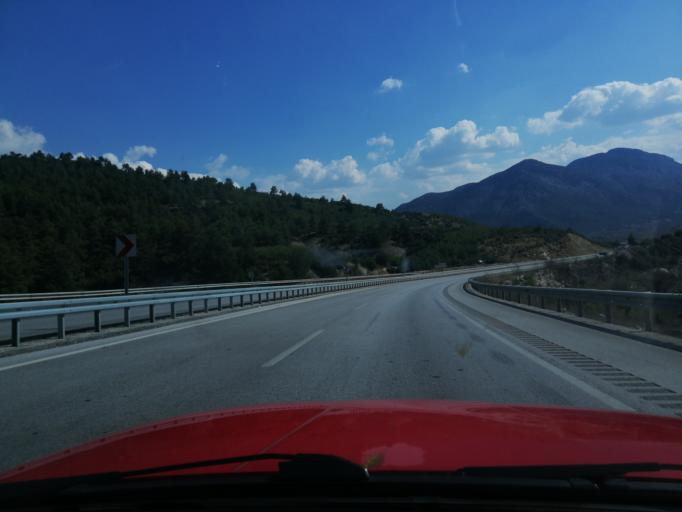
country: TR
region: Burdur
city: Celtikci
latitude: 37.5724
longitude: 30.4510
